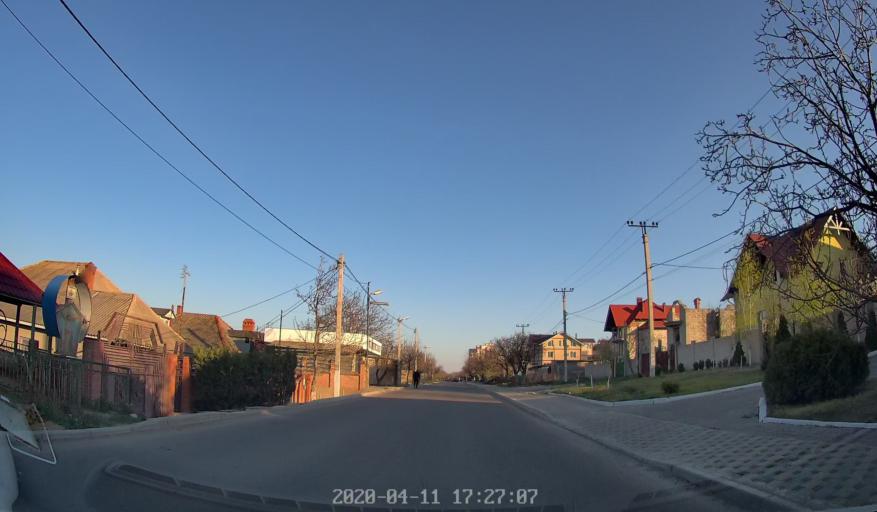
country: MD
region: Chisinau
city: Vatra
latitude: 47.0106
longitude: 28.7610
